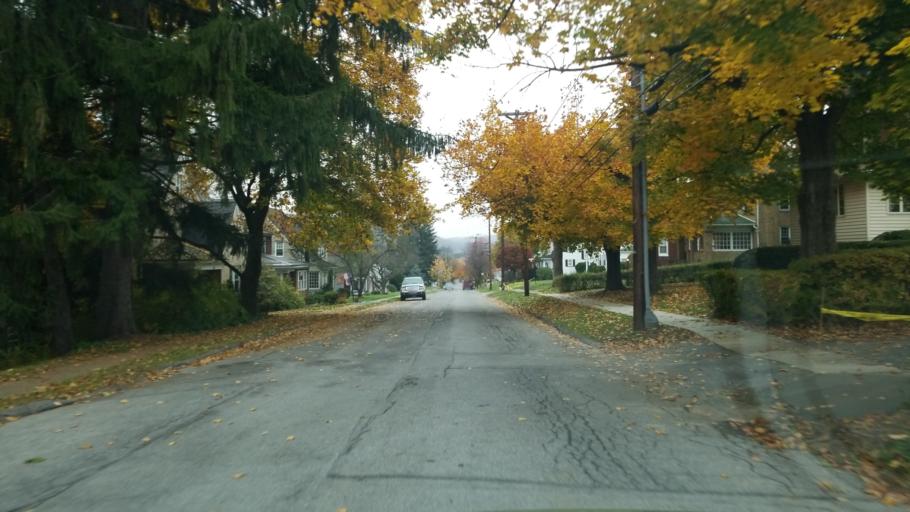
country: US
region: Pennsylvania
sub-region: Clearfield County
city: Clearfield
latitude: 41.0120
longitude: -78.4338
